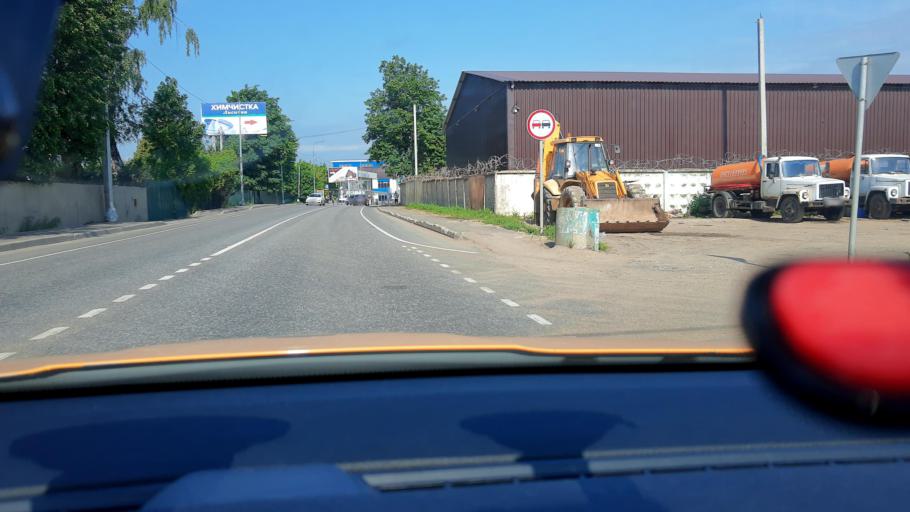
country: RU
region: Moskovskaya
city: Rozhdestveno
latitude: 55.8093
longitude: 37.0169
